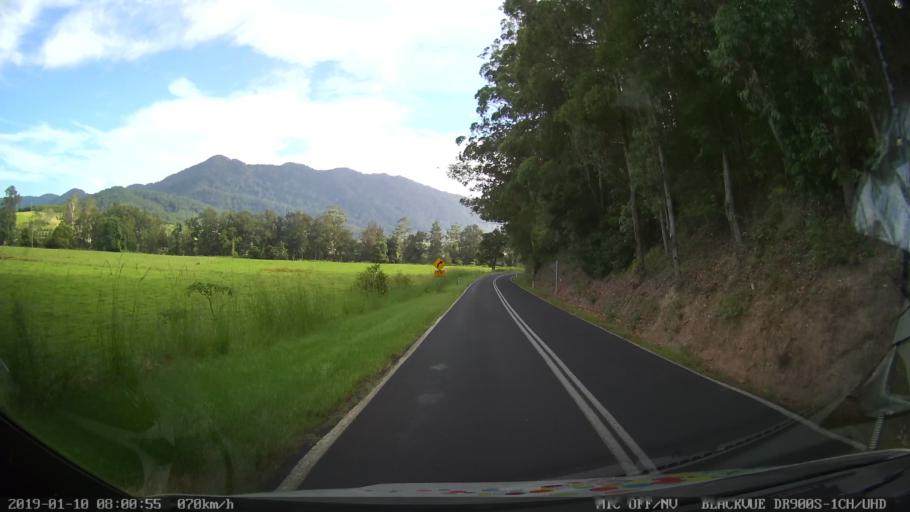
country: AU
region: New South Wales
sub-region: Bellingen
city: Dorrigo
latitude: -30.4246
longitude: 152.7876
